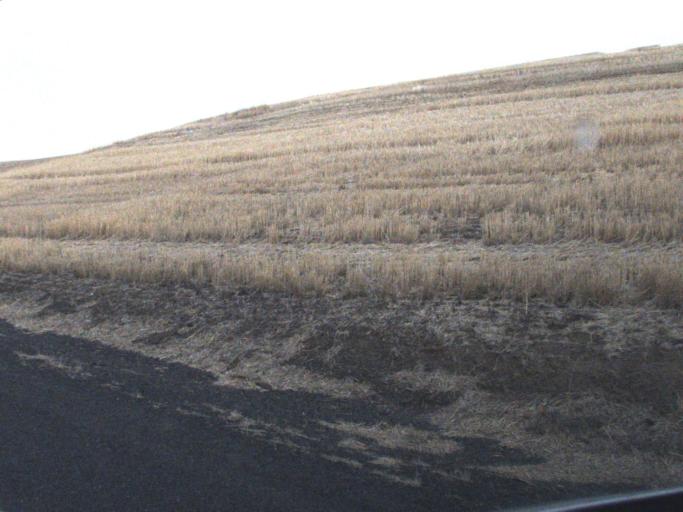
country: US
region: Washington
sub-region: Garfield County
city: Pomeroy
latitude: 46.8028
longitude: -117.7593
